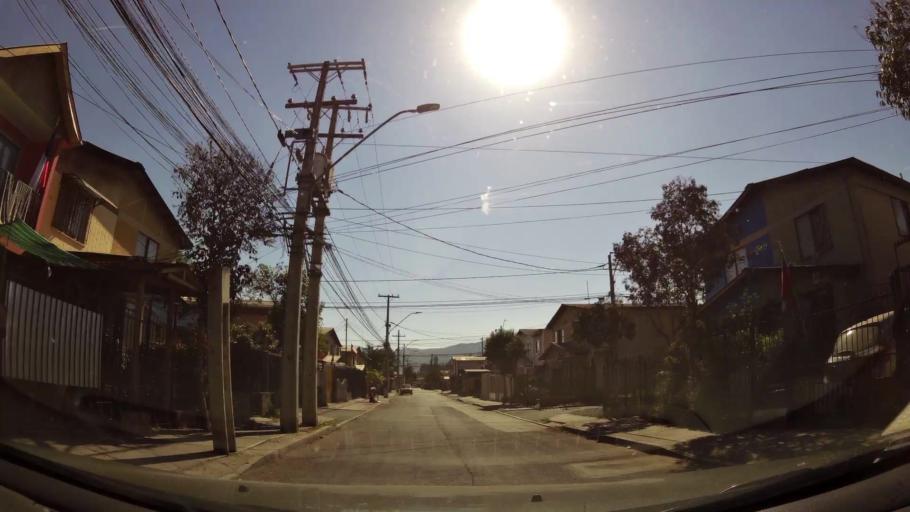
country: CL
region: Santiago Metropolitan
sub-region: Provincia de Maipo
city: San Bernardo
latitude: -33.6138
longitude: -70.7088
